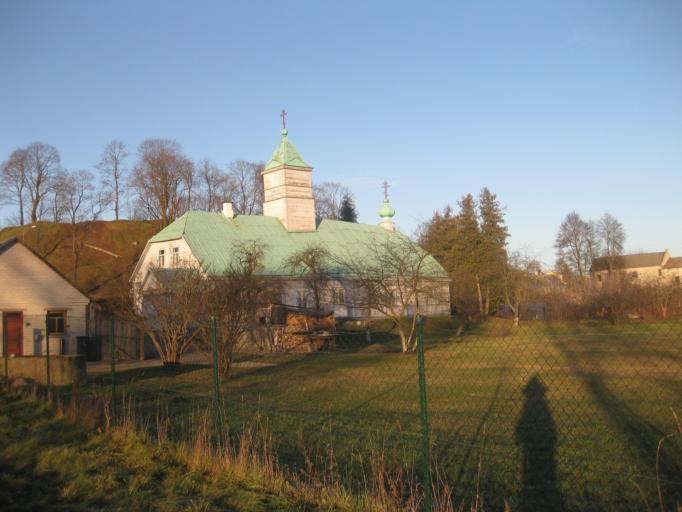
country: LT
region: Vilnius County
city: Ukmerge
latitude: 55.2493
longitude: 24.7690
